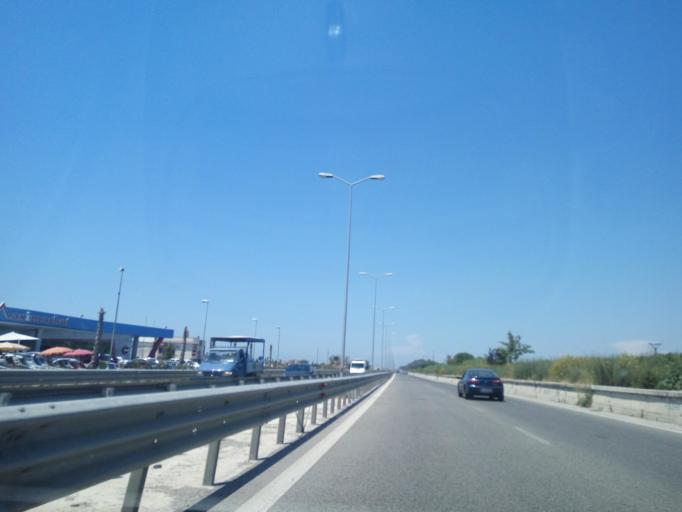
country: AL
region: Tirane
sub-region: Rrethi i Tiranes
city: Shengjergj
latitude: 41.2089
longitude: 19.5337
